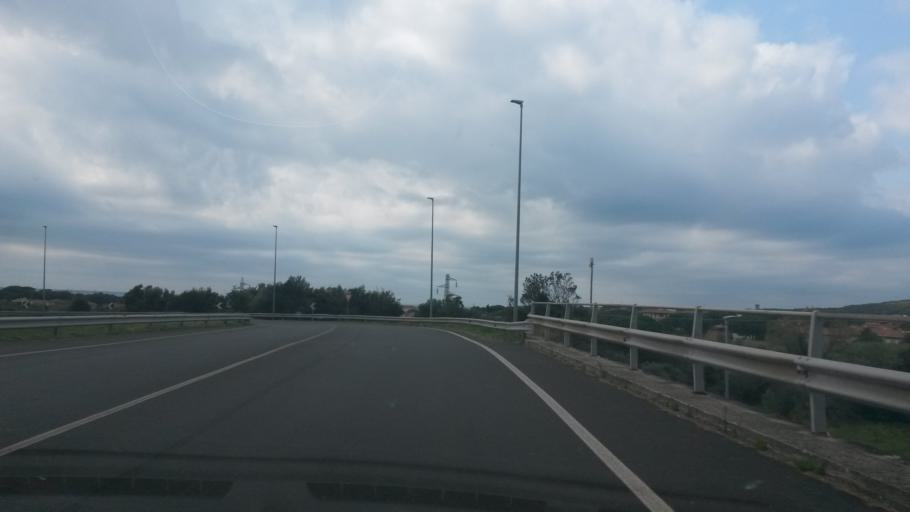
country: IT
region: Tuscany
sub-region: Provincia di Livorno
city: Rosignano Solvay-Castiglioncello
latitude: 43.4013
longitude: 10.4356
